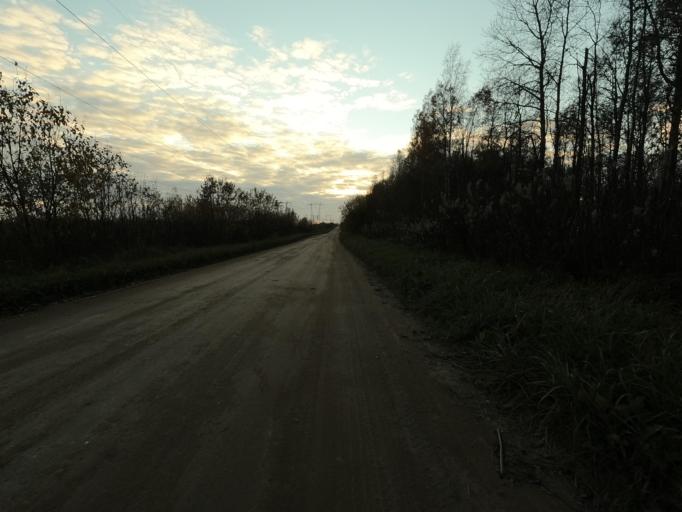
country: RU
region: Leningrad
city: Mga
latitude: 59.8066
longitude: 31.2004
